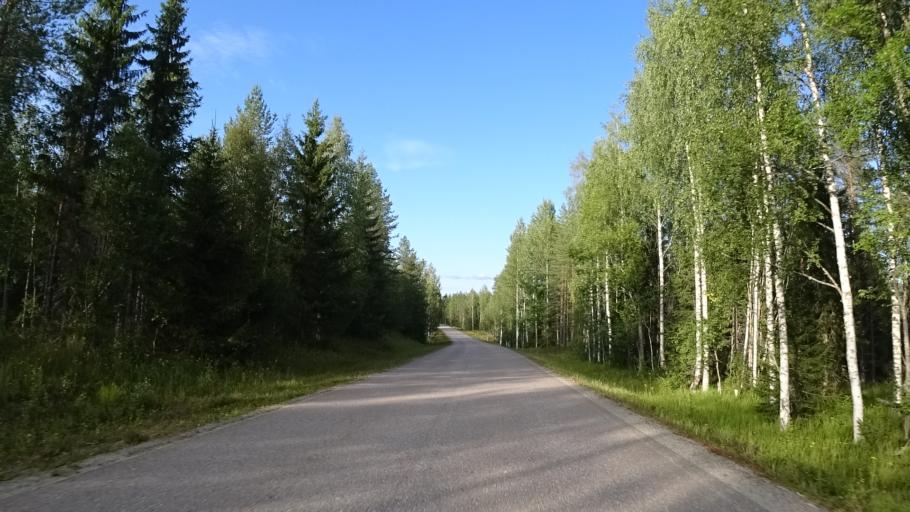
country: FI
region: North Karelia
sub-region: Joensuu
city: Eno
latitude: 63.0160
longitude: 30.4903
